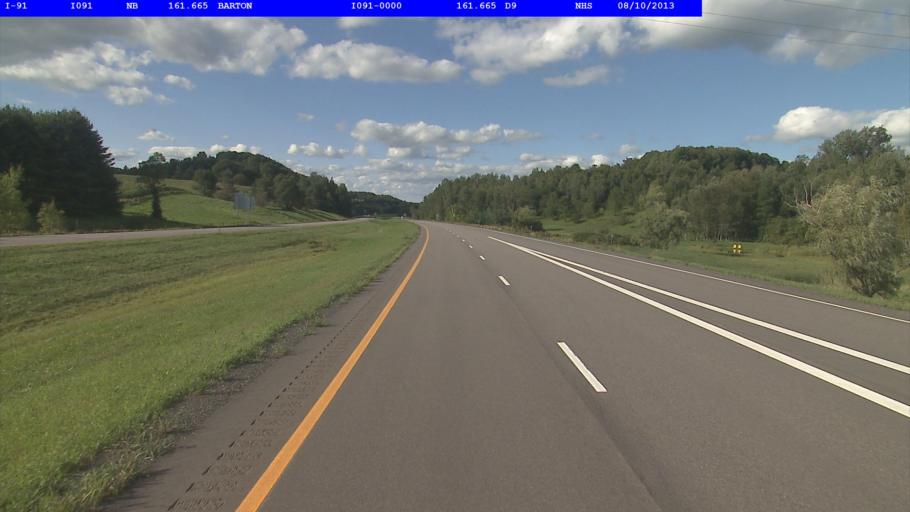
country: US
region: Vermont
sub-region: Orleans County
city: Newport
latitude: 44.8101
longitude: -72.2110
